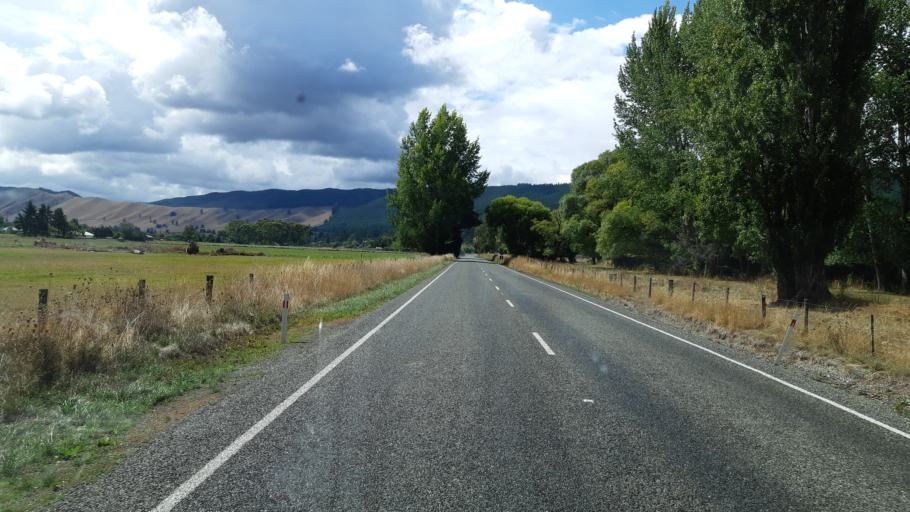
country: NZ
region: Tasman
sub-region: Tasman District
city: Wakefield
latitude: -41.4517
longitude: 172.8228
